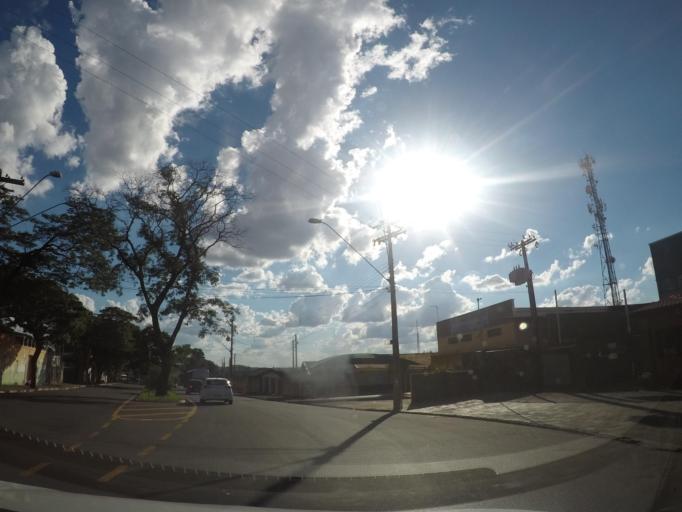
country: BR
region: Sao Paulo
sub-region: Sumare
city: Sumare
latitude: -22.8052
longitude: -47.2238
